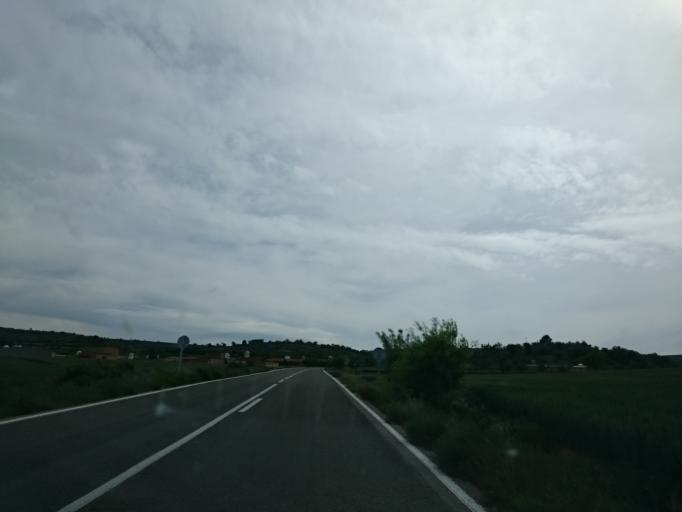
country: ES
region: Catalonia
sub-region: Provincia de Lleida
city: Ivorra
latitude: 41.7765
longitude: 1.3892
